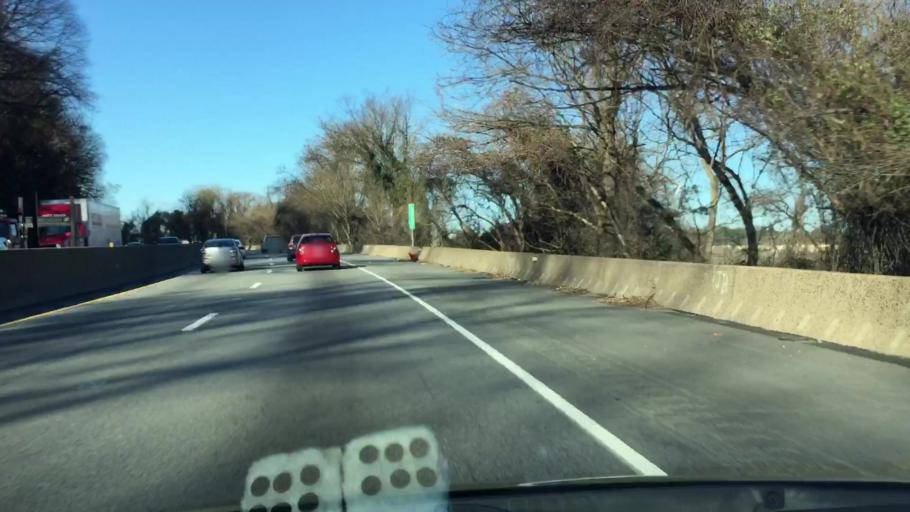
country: US
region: Pennsylvania
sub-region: Montgomery County
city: Conshohocken
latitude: 40.0707
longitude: -75.2812
